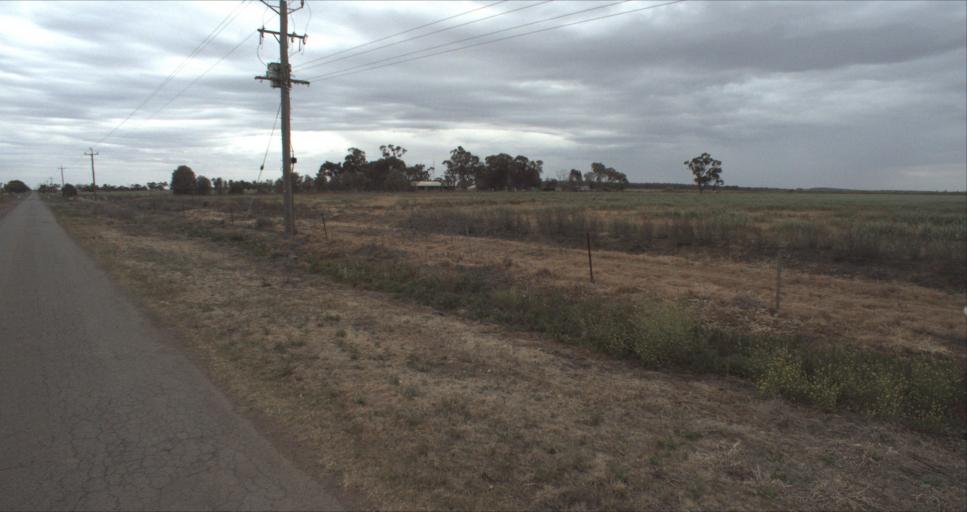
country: AU
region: New South Wales
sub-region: Leeton
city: Leeton
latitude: -34.4070
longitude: 146.3411
